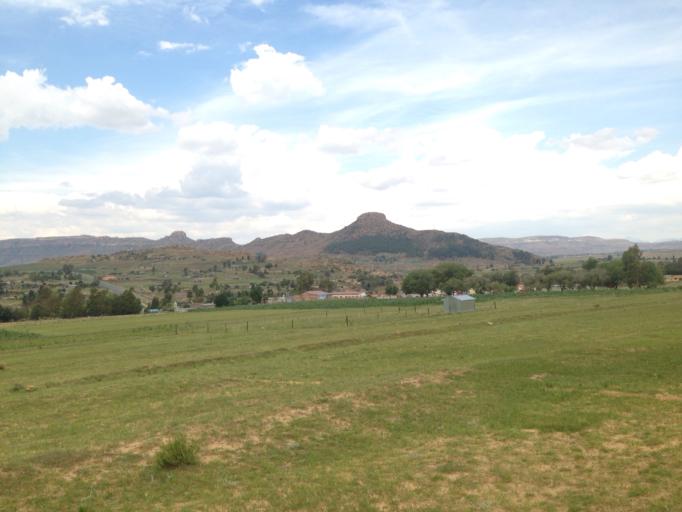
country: LS
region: Mafeteng
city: Mafeteng
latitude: -29.6914
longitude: 27.4320
